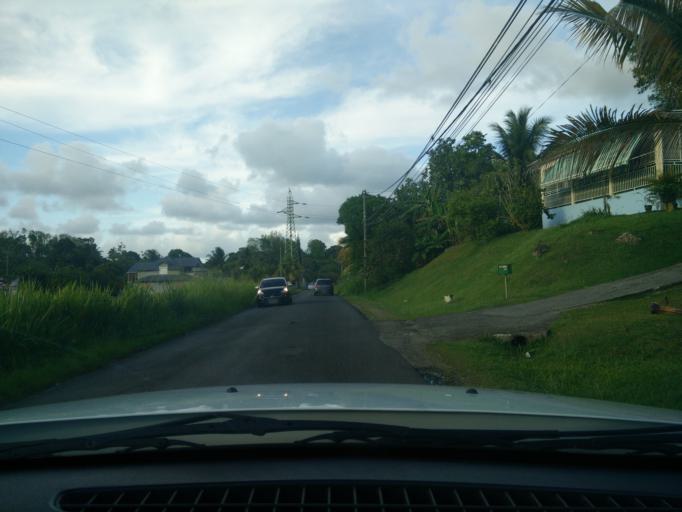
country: GP
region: Guadeloupe
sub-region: Guadeloupe
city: Les Abymes
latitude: 16.2531
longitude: -61.5067
